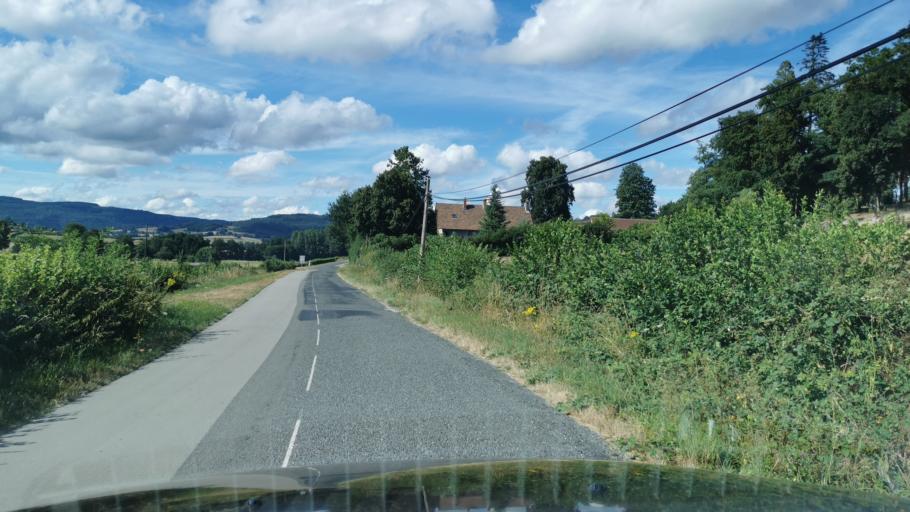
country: FR
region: Bourgogne
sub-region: Departement de Saone-et-Loire
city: Marmagne
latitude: 46.8368
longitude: 4.3189
